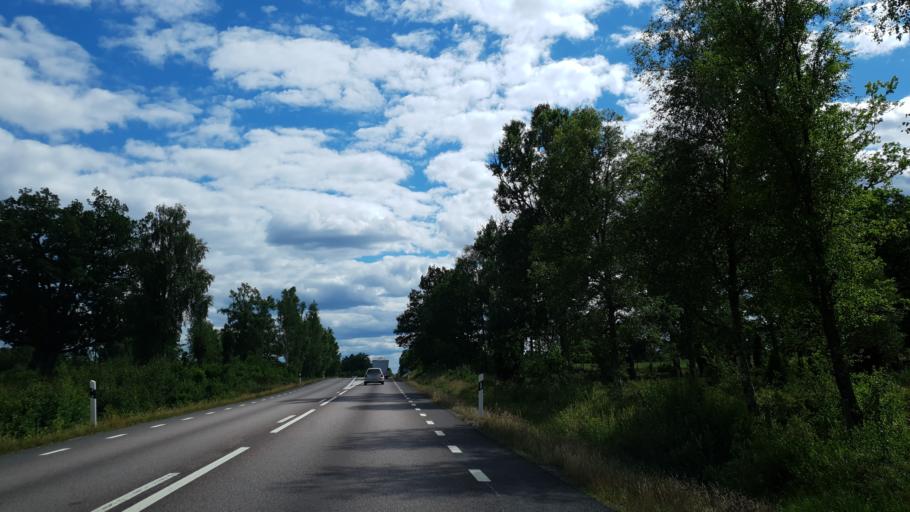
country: SE
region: Kronoberg
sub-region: Lessebo Kommun
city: Lessebo
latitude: 56.8604
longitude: 15.3878
